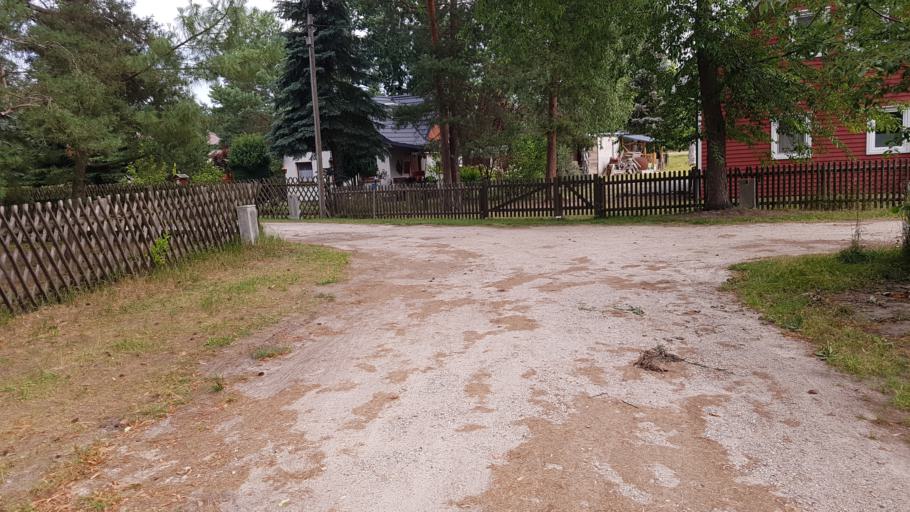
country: DE
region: Brandenburg
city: Gross Koris
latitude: 52.1732
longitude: 13.7034
